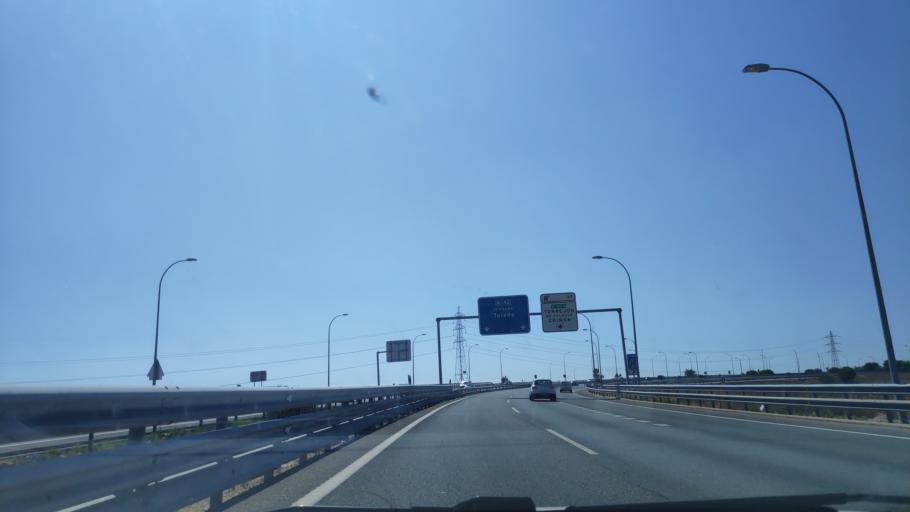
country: ES
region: Madrid
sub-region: Provincia de Madrid
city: Torrejon de la Calzada
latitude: 40.2006
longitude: -3.7891
